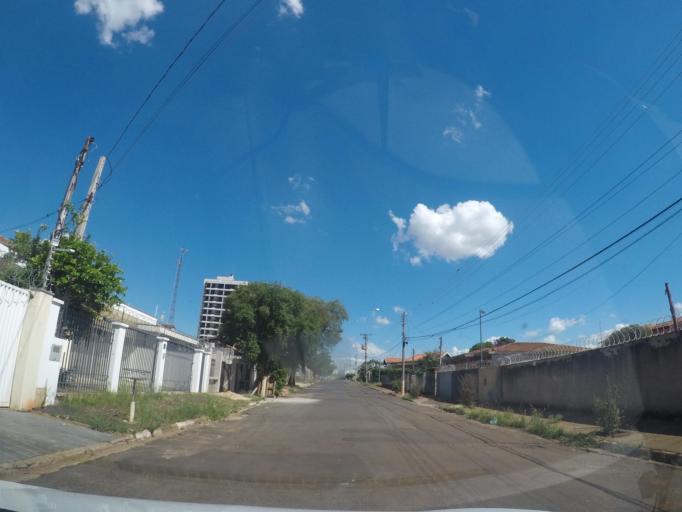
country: BR
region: Sao Paulo
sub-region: Sumare
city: Sumare
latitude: -22.8280
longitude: -47.2686
